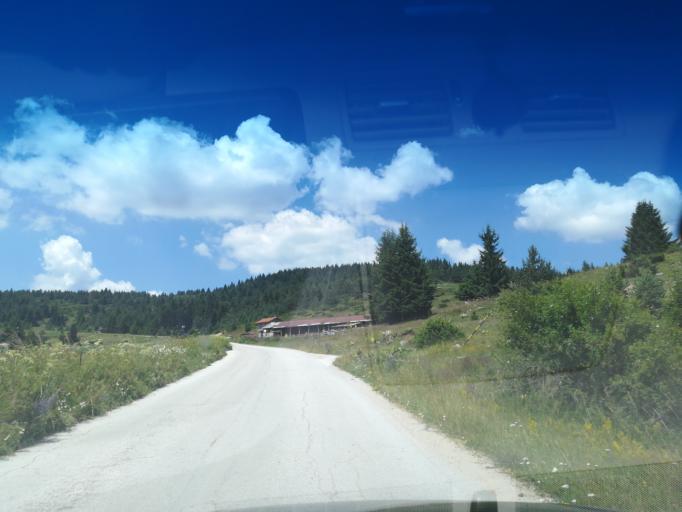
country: BG
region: Smolyan
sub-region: Obshtina Chepelare
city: Chepelare
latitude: 41.6964
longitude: 24.7815
